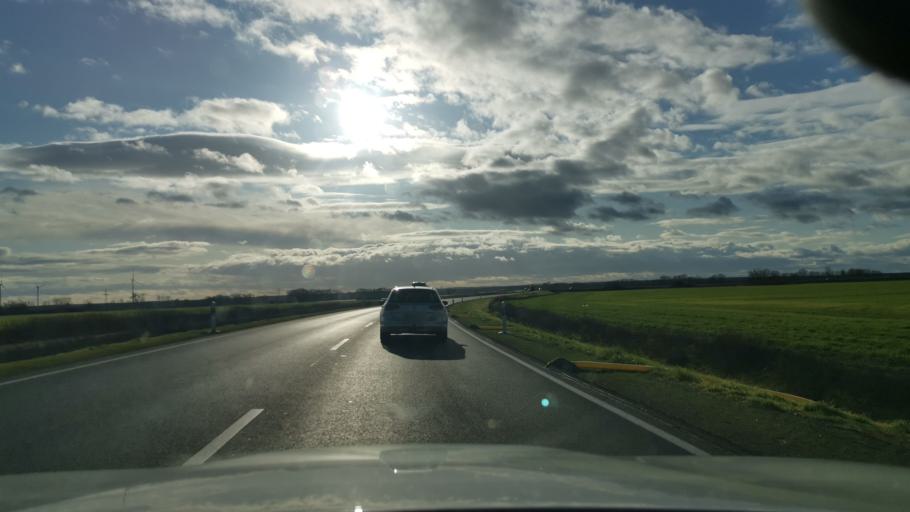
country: DE
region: Saxony-Anhalt
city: Kemberg
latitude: 51.8181
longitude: 12.6457
